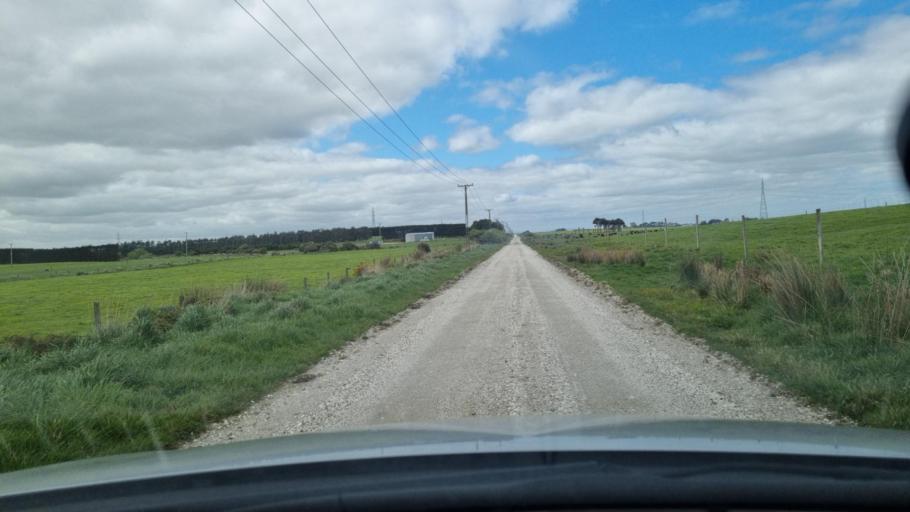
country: NZ
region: Southland
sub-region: Invercargill City
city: Invercargill
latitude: -46.4429
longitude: 168.4320
